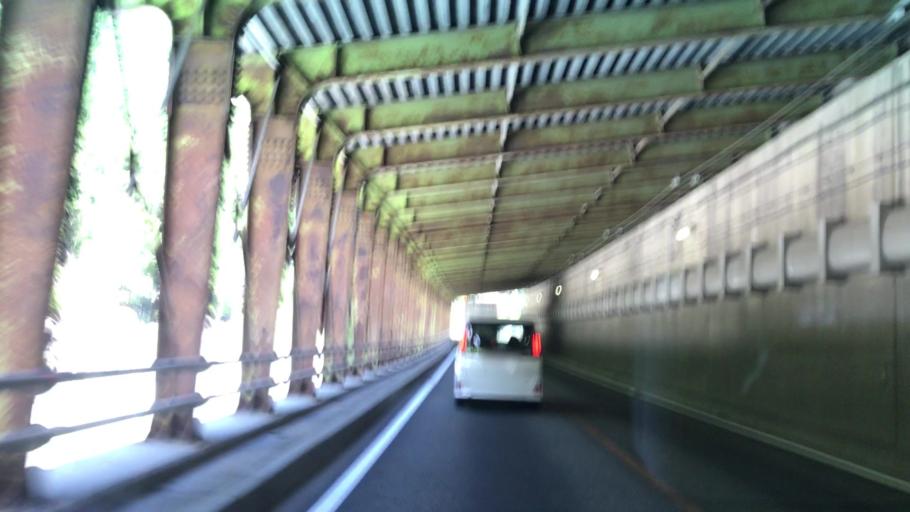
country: JP
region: Hokkaido
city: Shimo-furano
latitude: 42.9437
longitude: 142.5989
